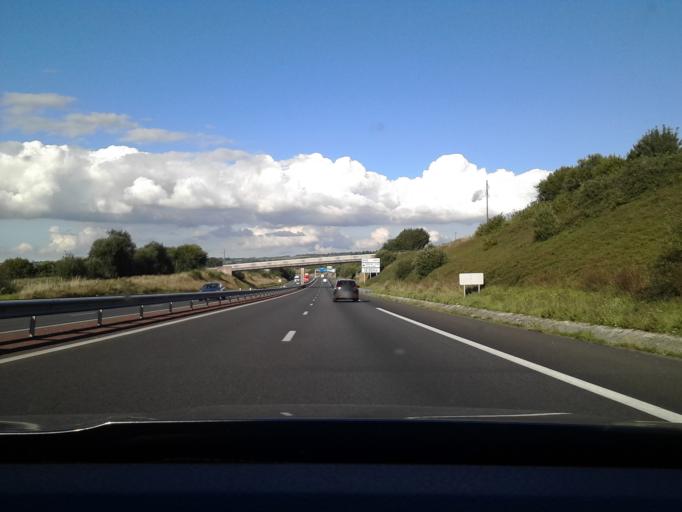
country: FR
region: Lower Normandy
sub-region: Departement de la Manche
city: Torigni-sur-Vire
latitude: 48.9722
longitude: -0.9636
